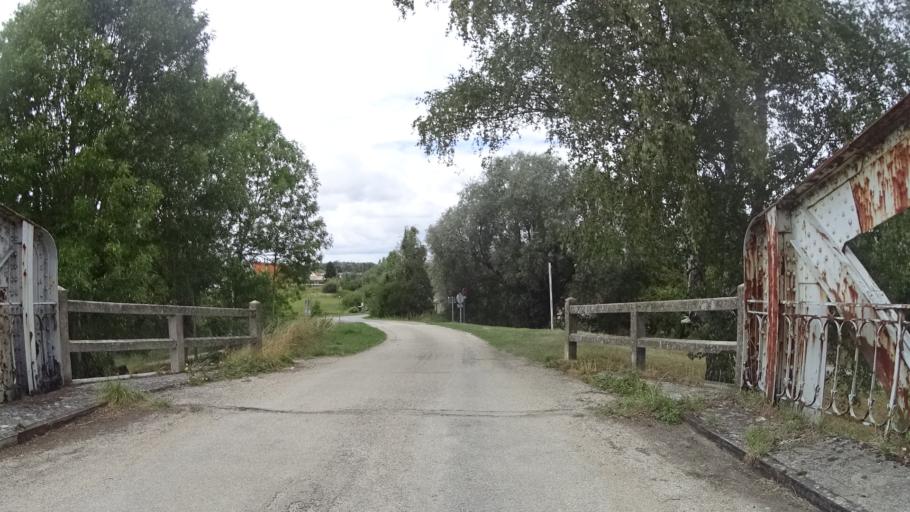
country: FR
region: Picardie
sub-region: Departement de l'Aisne
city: Viry-Noureuil
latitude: 49.6175
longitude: 3.2427
